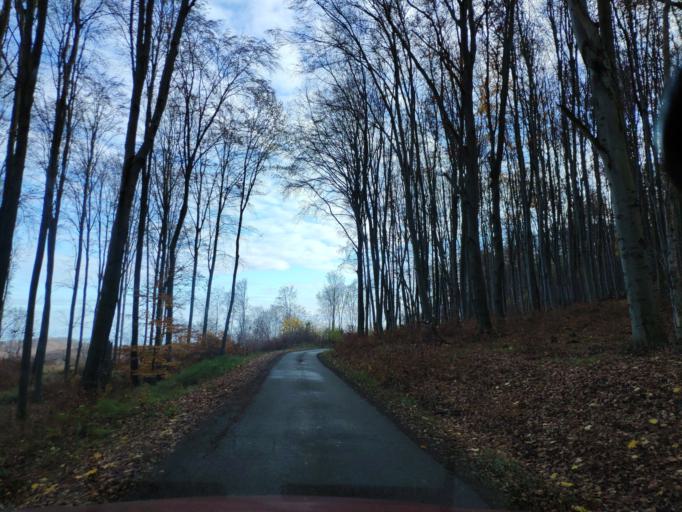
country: HU
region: Borsod-Abauj-Zemplen
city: Gonc
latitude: 48.5864
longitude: 21.4679
